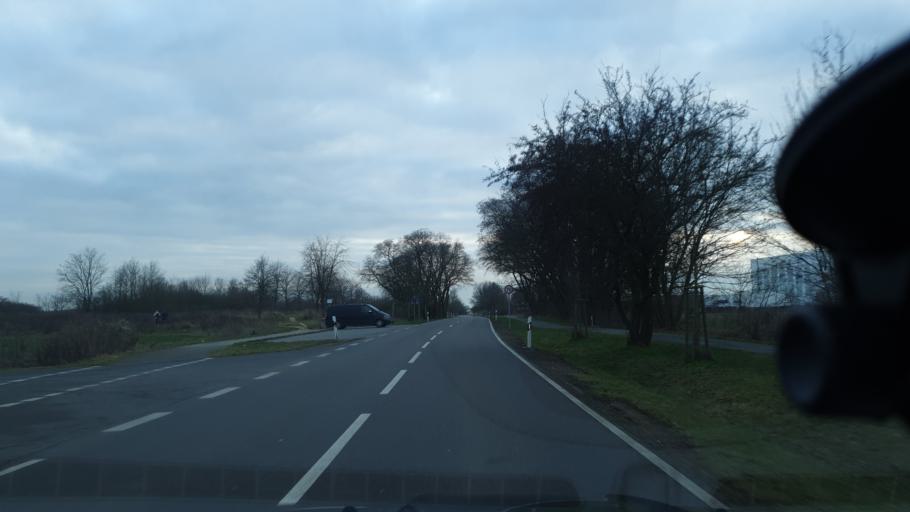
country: DE
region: Brandenburg
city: Schulzendorf
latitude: 52.3750
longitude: 13.5708
